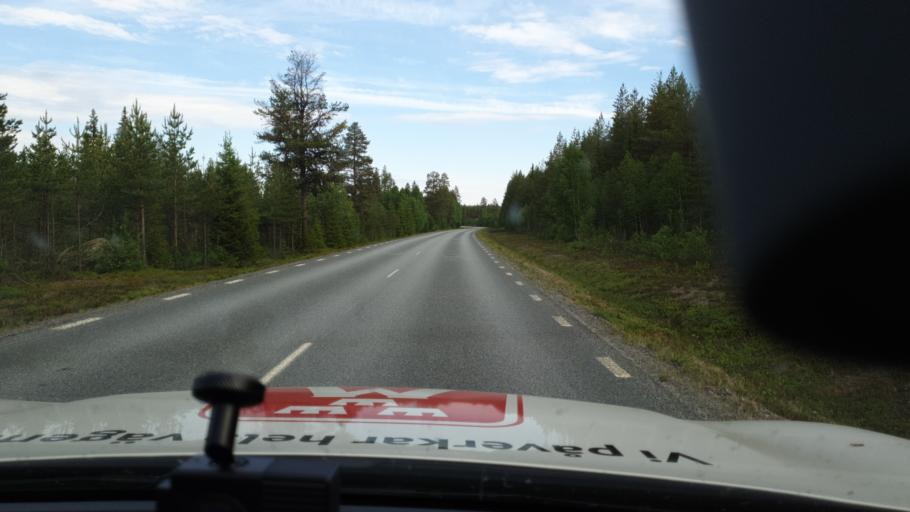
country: SE
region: Vaesterbotten
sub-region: Lycksele Kommun
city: Soderfors
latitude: 65.1426
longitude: 18.2645
